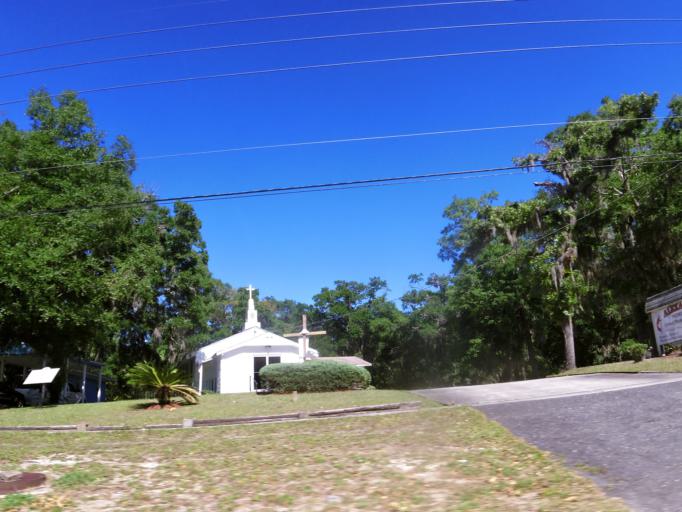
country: US
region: Florida
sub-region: Duval County
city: Atlantic Beach
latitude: 30.3617
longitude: -81.5156
